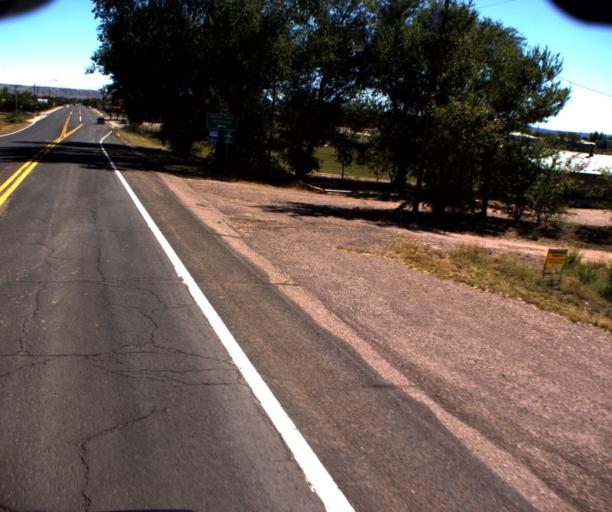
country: US
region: Arizona
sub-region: Apache County
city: Saint Johns
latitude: 34.5064
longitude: -109.3868
